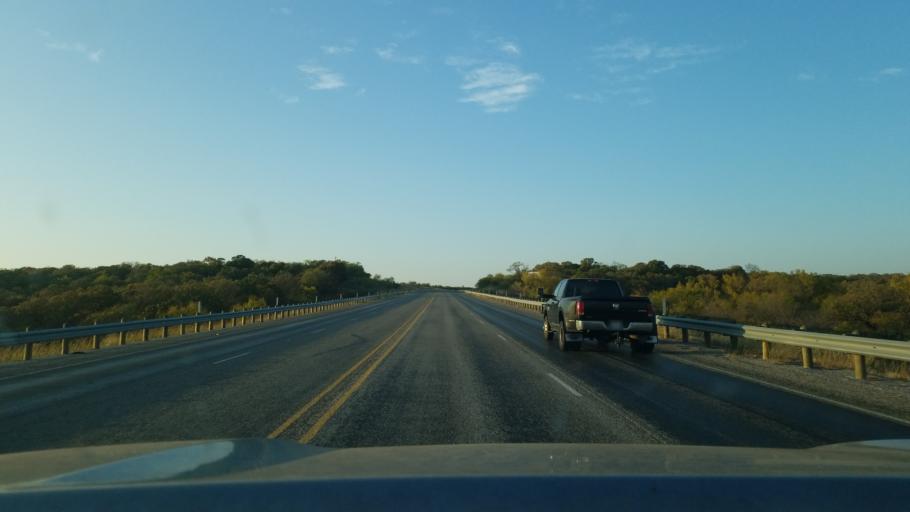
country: US
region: Texas
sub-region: Eastland County
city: Cisco
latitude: 32.3544
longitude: -98.9664
